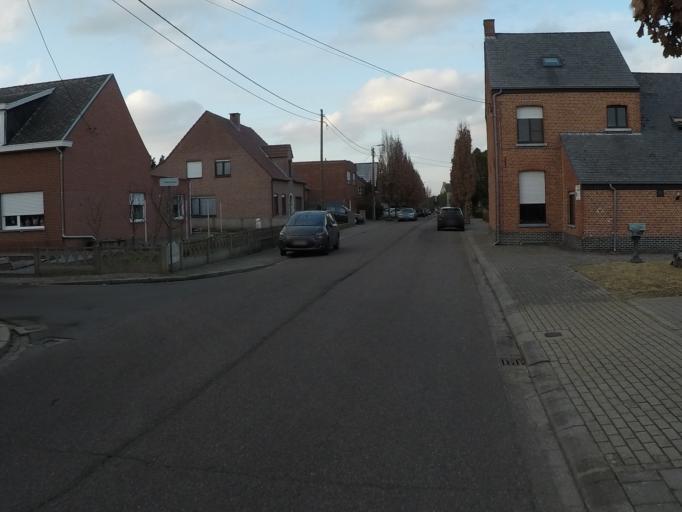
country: BE
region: Flanders
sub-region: Provincie Antwerpen
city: Putte
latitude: 51.0553
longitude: 4.6352
